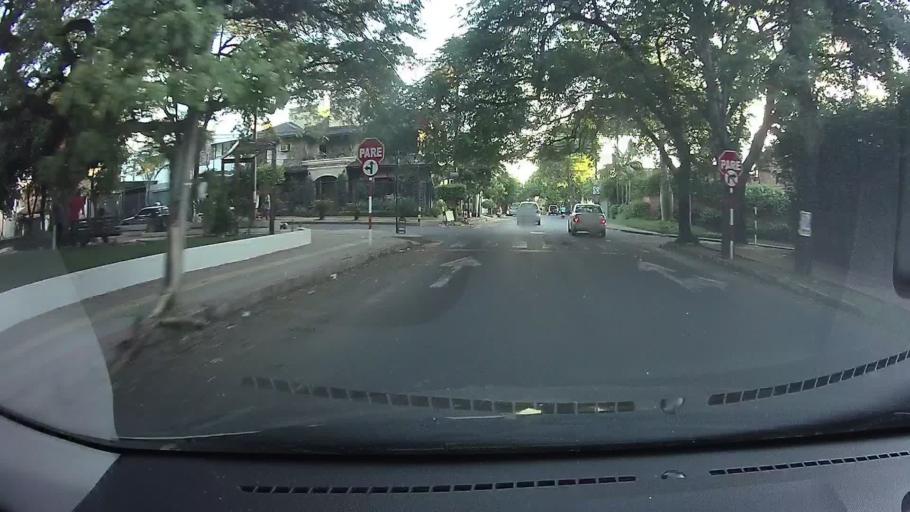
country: PY
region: Central
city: Lambare
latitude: -25.3088
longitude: -57.5782
